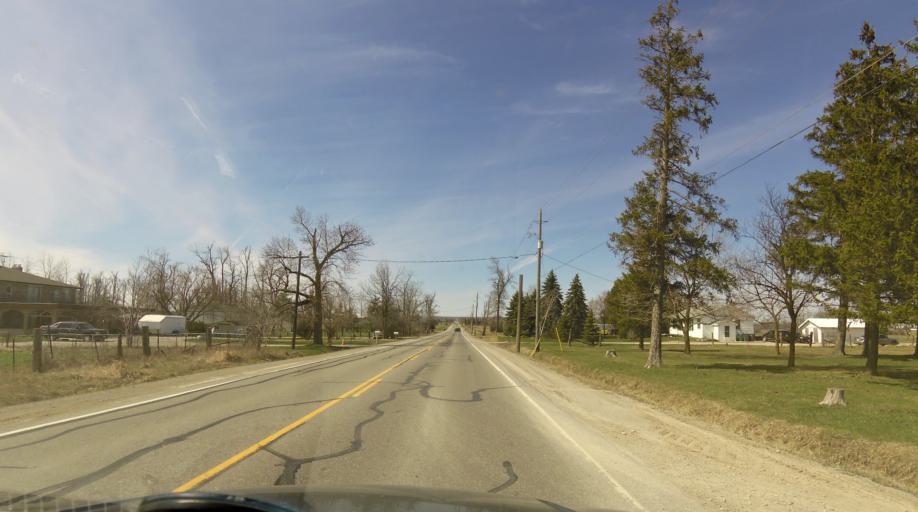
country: CA
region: Ontario
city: Brampton
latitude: 43.6969
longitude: -79.8702
